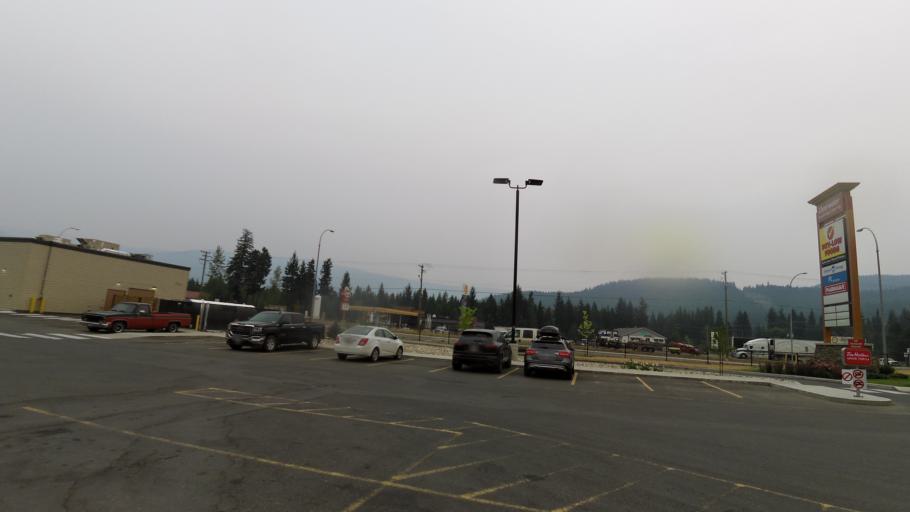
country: CA
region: British Columbia
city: Chase
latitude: 51.6504
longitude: -120.0395
